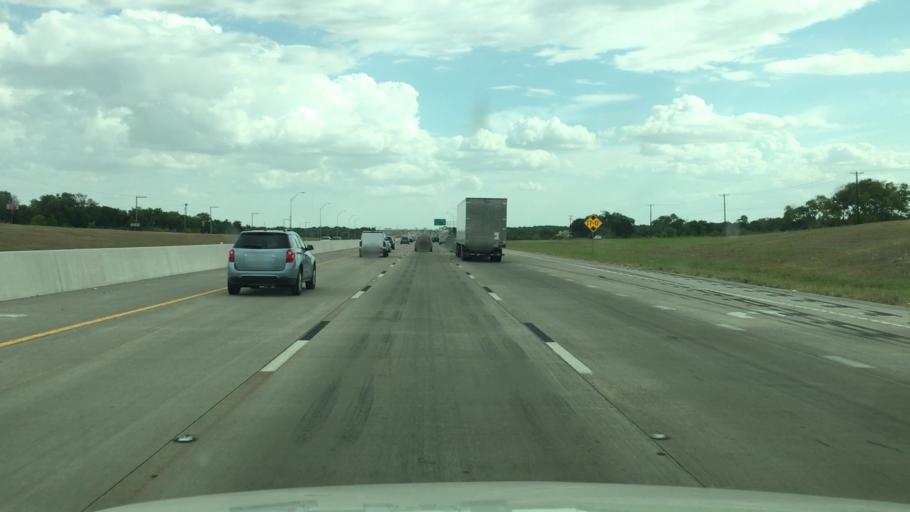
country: US
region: Texas
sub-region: McLennan County
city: Lorena
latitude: 31.3797
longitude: -97.2140
